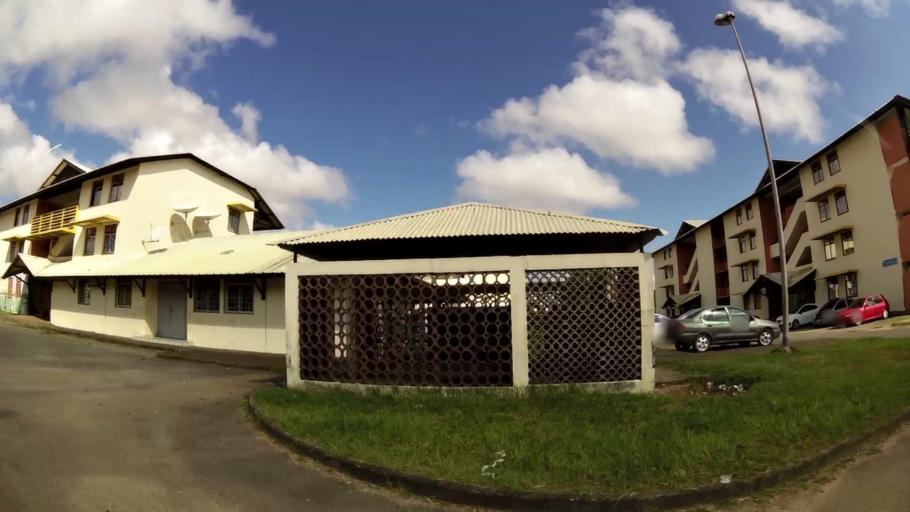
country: GF
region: Guyane
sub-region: Guyane
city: Cayenne
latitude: 4.9357
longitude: -52.3160
